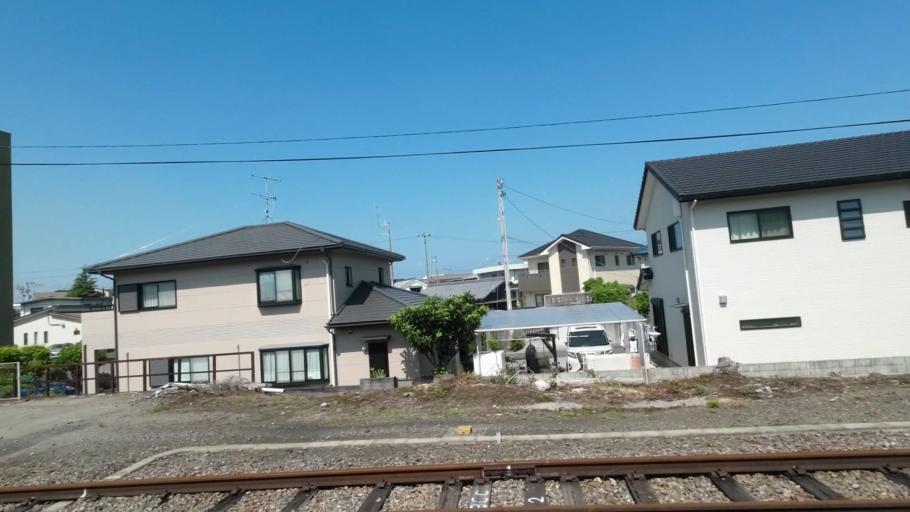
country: JP
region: Ehime
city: Kawanoecho
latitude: 34.0156
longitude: 133.5763
